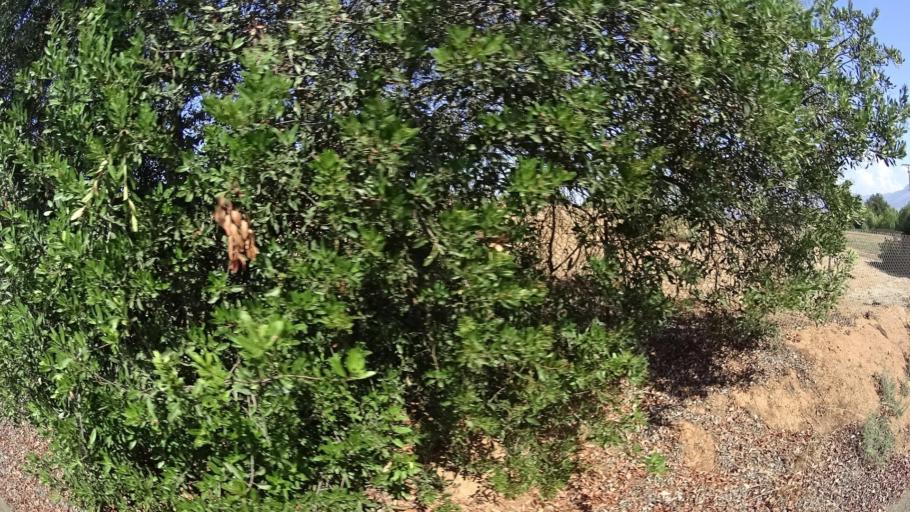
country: US
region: California
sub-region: San Diego County
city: Valley Center
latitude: 33.2908
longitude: -117.0266
